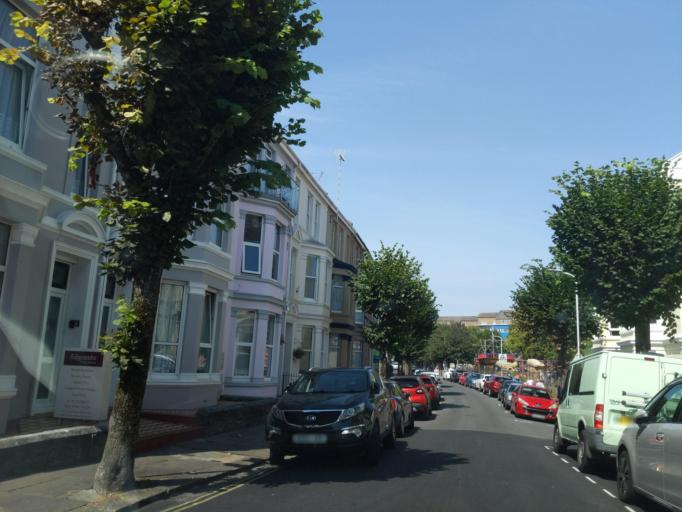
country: GB
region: England
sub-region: Plymouth
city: Plymouth
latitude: 50.3641
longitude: -4.1475
